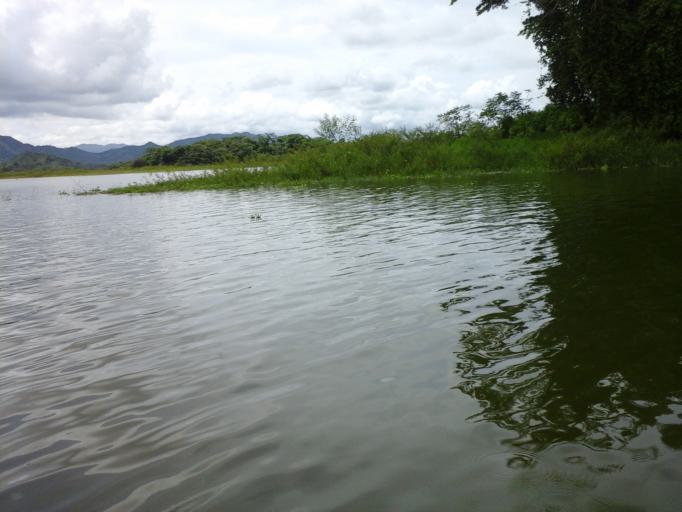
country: CO
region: Bolivar
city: San Cristobal
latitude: 9.8733
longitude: -75.3000
